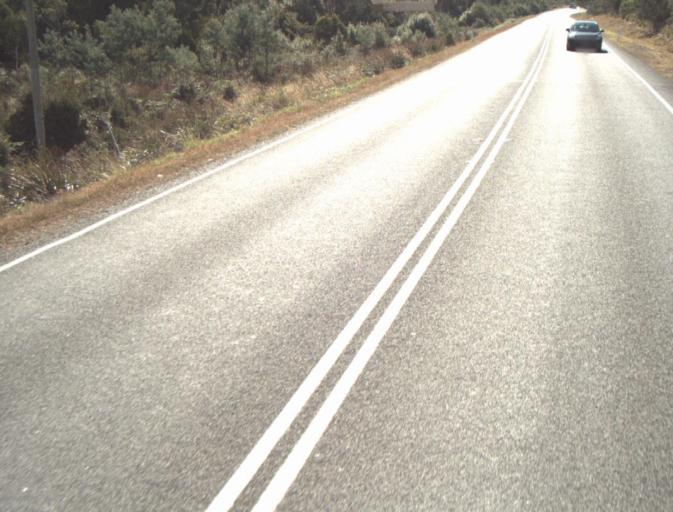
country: AU
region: Tasmania
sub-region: Launceston
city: Mayfield
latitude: -41.3632
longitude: 147.1449
